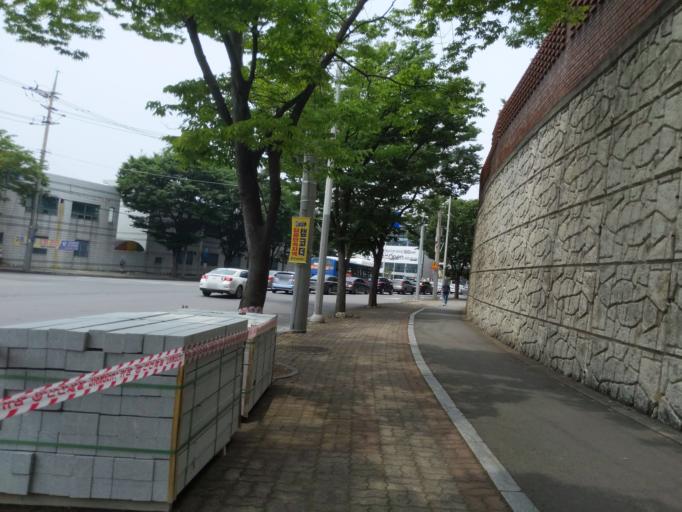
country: KR
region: Daegu
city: Hwawon
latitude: 35.8077
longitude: 128.5286
